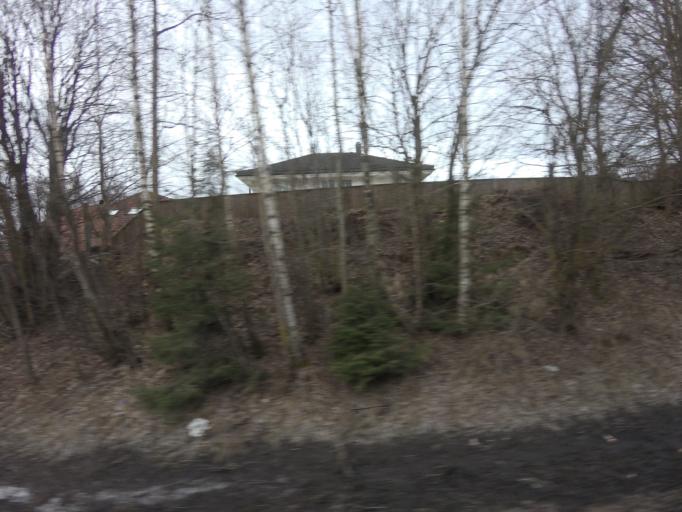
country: NO
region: Akershus
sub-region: Skedsmo
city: Lillestrom
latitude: 59.9952
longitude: 11.0475
